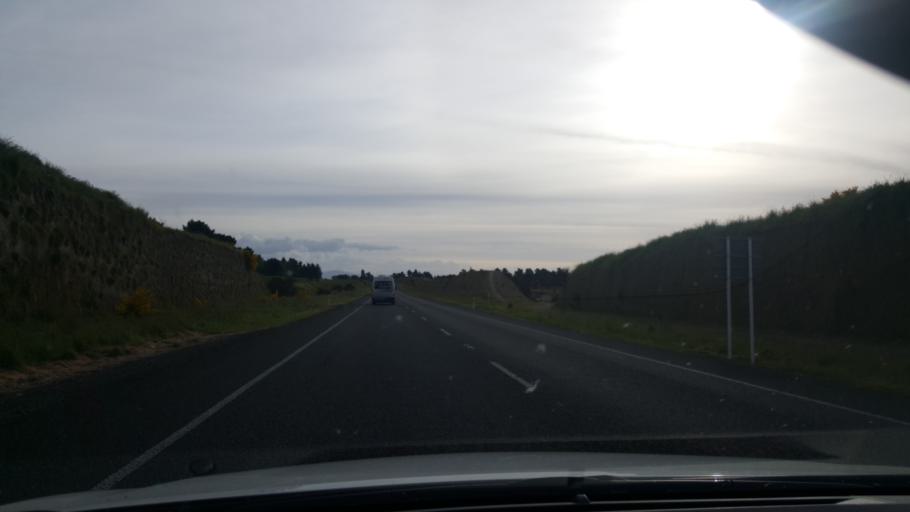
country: NZ
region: Waikato
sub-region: Taupo District
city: Taupo
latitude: -38.7323
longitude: 176.0816
